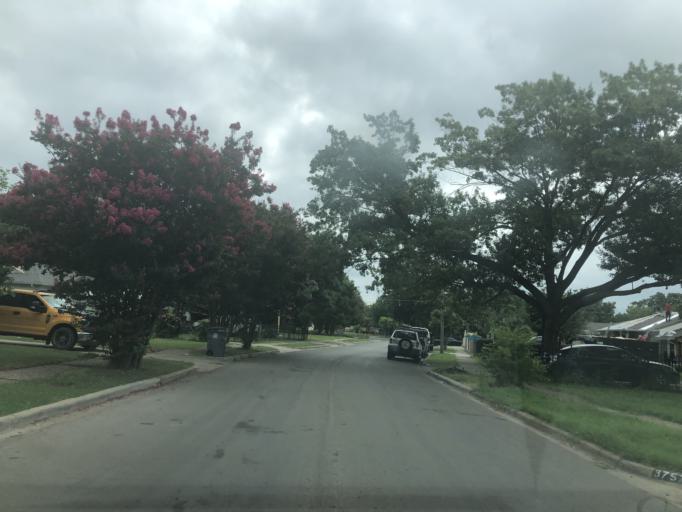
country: US
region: Texas
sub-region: Dallas County
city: University Park
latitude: 32.8645
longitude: -96.8540
